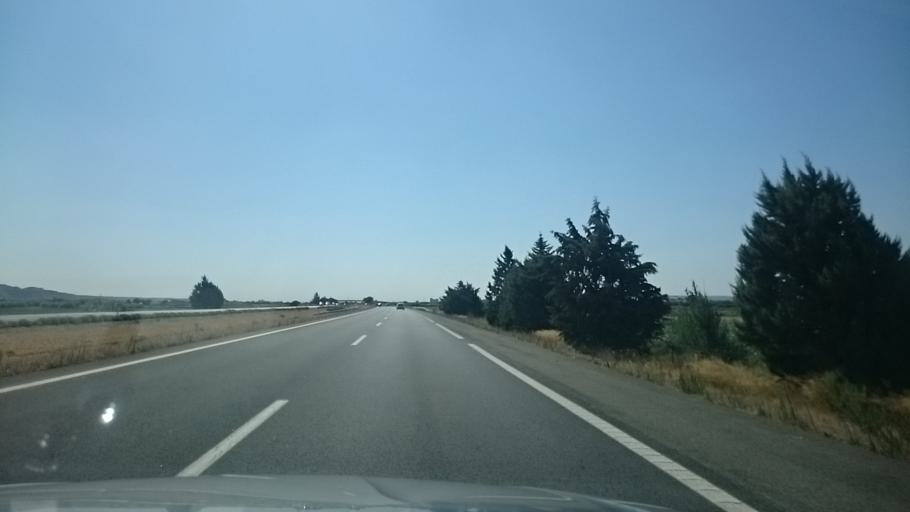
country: ES
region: Aragon
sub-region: Provincia de Zaragoza
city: Torres de Berrellen
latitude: 41.7491
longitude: -1.0666
